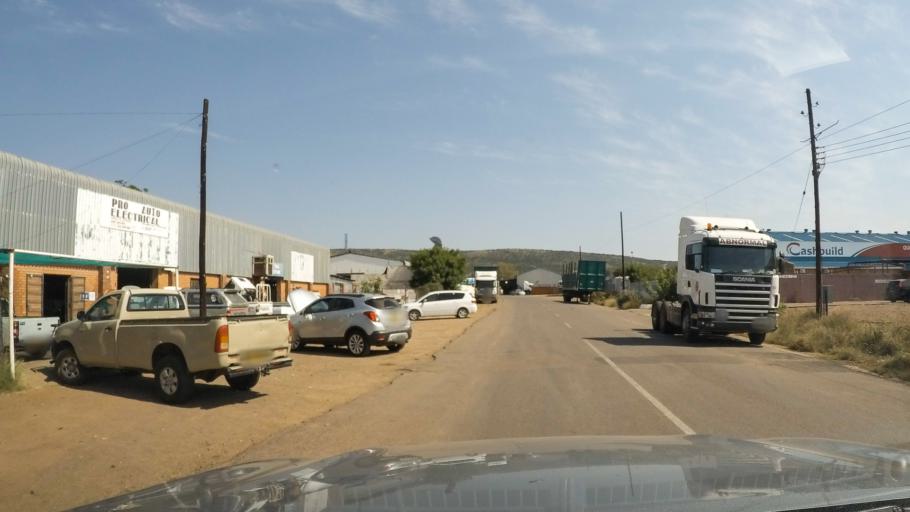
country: BW
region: South East
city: Lobatse
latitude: -25.2025
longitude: 25.6843
